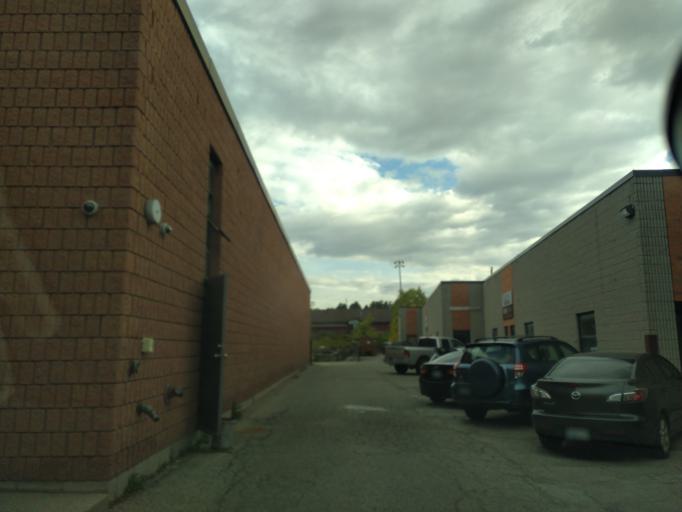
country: CA
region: Ontario
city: Newmarket
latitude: 43.9840
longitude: -79.4610
